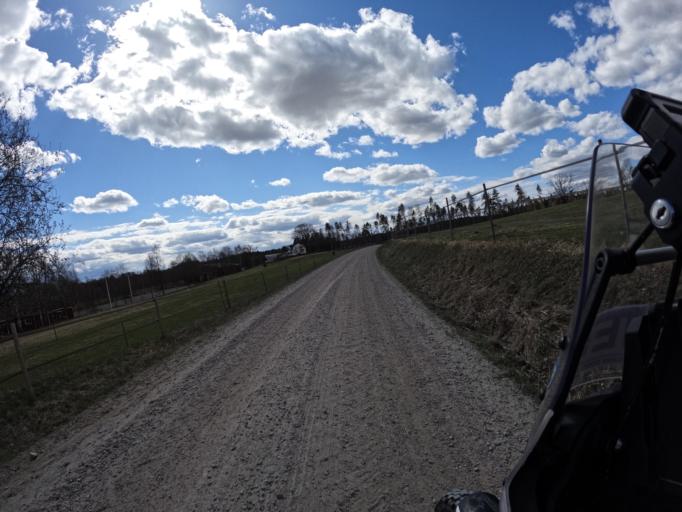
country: SE
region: Vaestra Goetaland
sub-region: Falkopings Kommun
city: Floby
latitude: 57.9617
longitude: 13.3060
